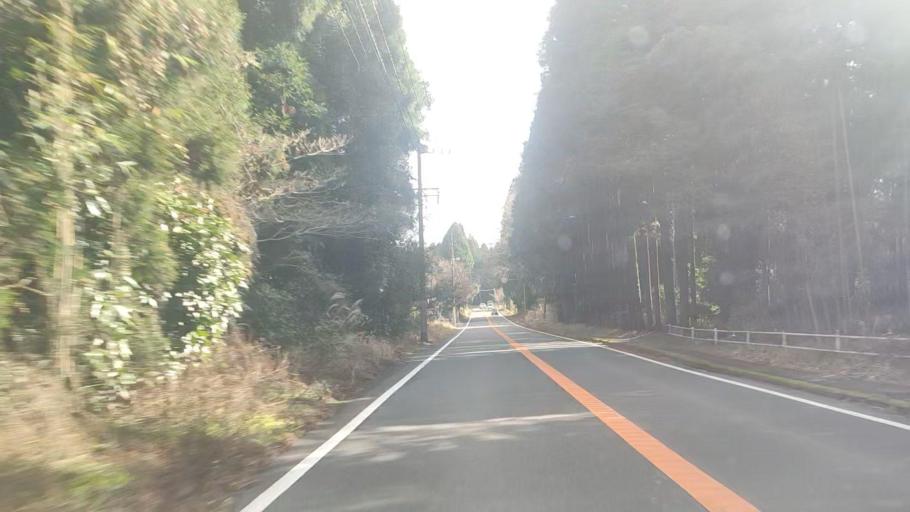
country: JP
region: Kagoshima
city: Kajiki
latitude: 31.8258
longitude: 130.6898
